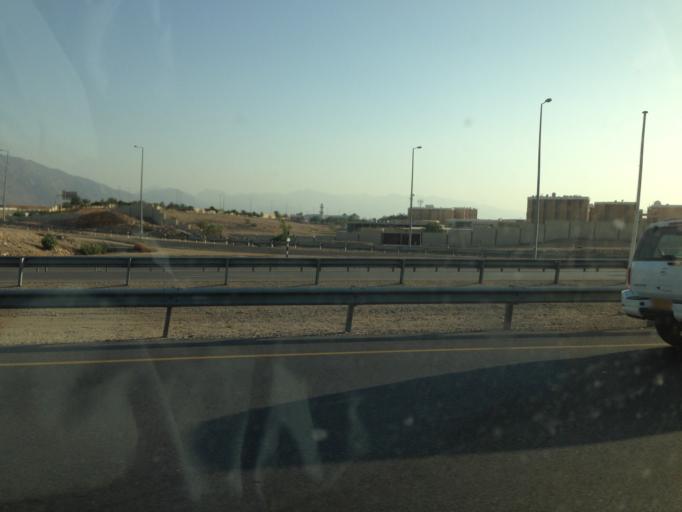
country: OM
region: Muhafazat Masqat
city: Bawshar
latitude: 23.5675
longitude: 58.3770
